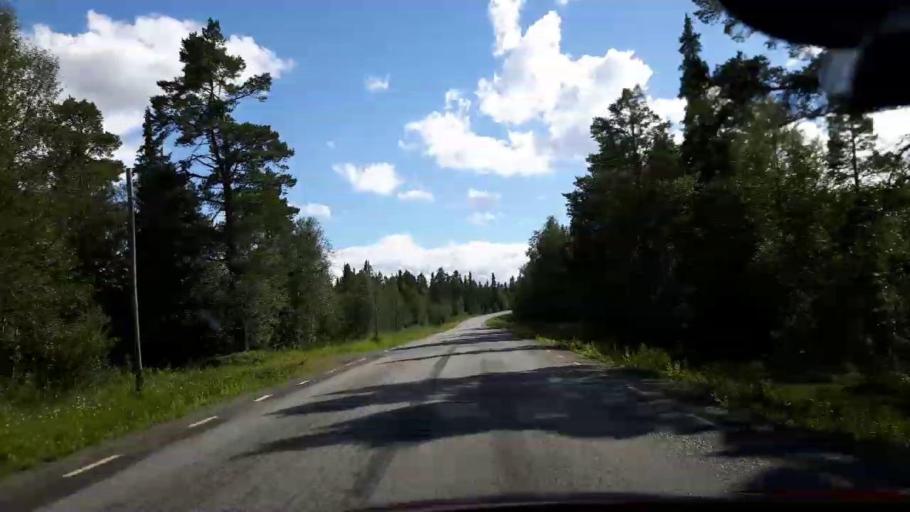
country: SE
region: Jaemtland
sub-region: Are Kommun
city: Are
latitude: 63.2185
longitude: 13.1644
